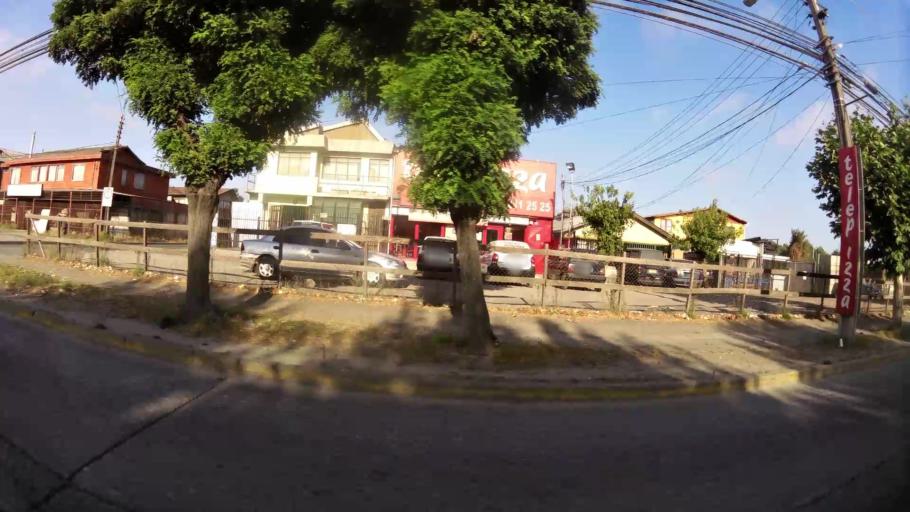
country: CL
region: Biobio
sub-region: Provincia de Concepcion
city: Concepcion
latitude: -36.7885
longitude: -73.0868
